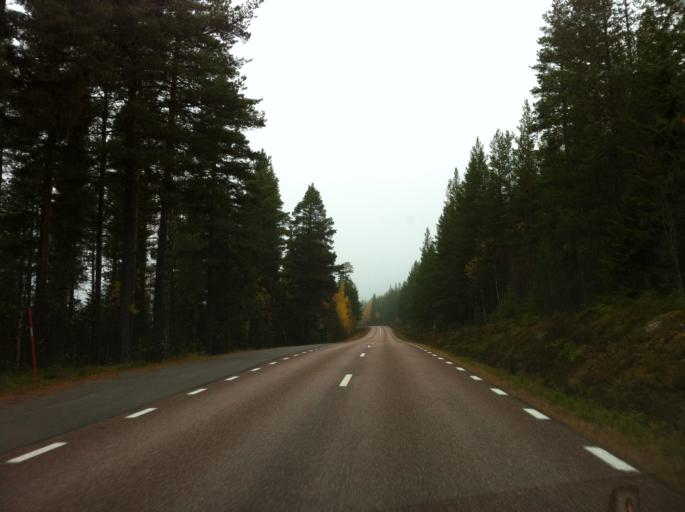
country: NO
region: Hedmark
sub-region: Trysil
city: Innbygda
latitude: 61.7804
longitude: 12.9406
